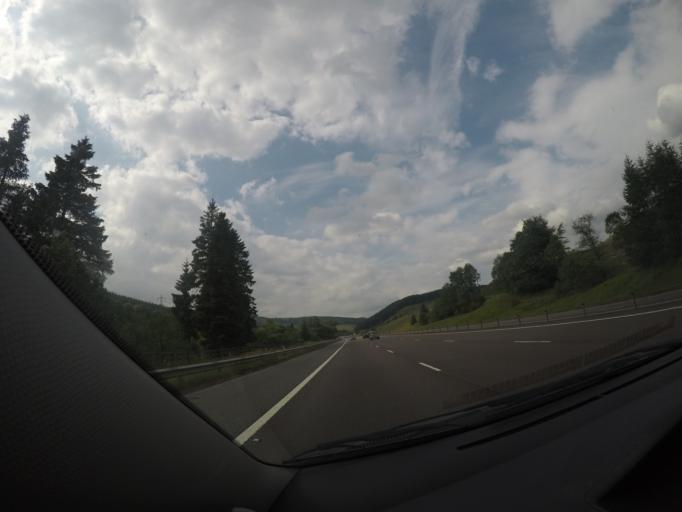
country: GB
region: Scotland
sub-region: Dumfries and Galloway
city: Moffat
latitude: 55.3522
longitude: -3.5077
